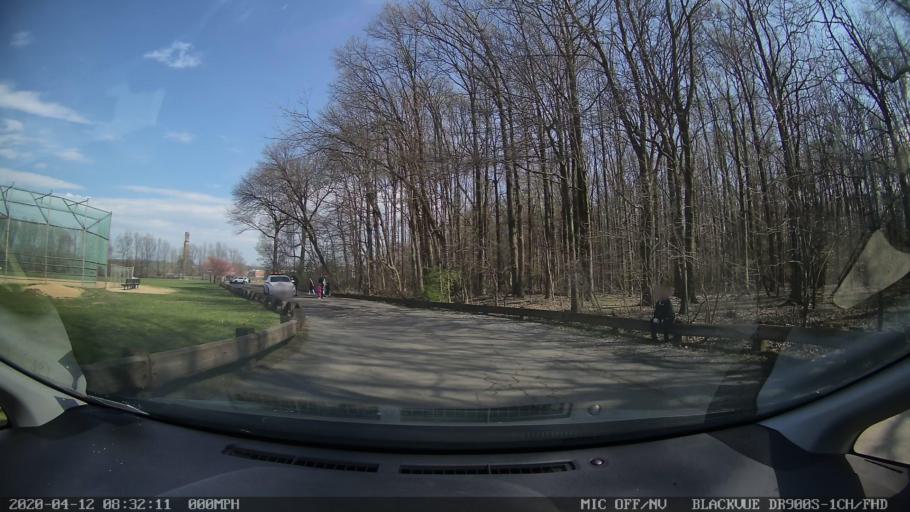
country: US
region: New York
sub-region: Richmond County
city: Bloomfield
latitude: 40.6058
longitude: -74.1571
